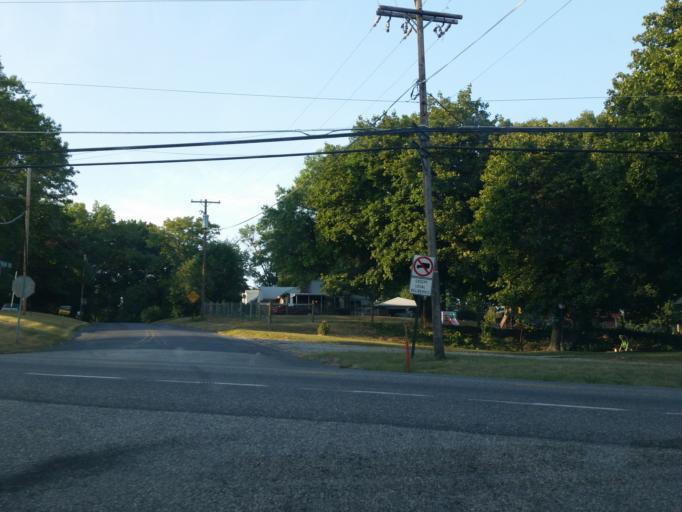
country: US
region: Pennsylvania
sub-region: Lebanon County
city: Annville
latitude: 40.3493
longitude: -76.5276
